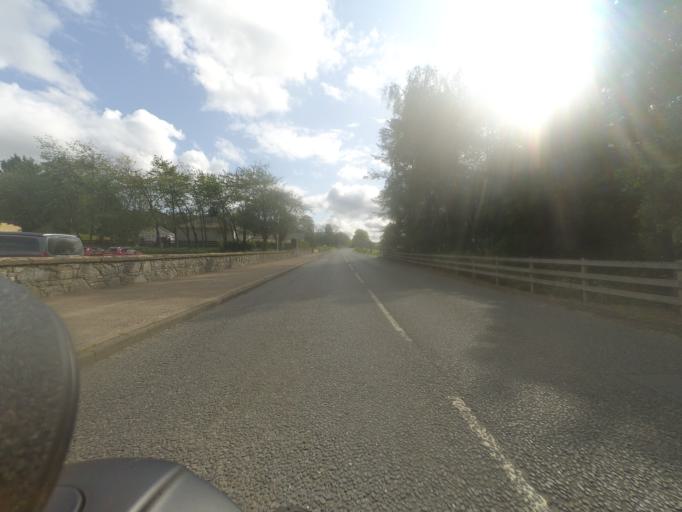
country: GB
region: Scotland
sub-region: Moray
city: Dufftown
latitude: 57.4531
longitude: -3.1304
